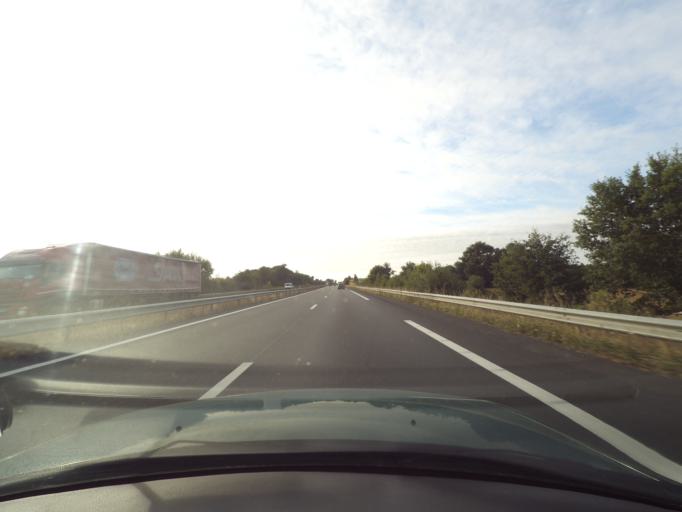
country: FR
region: Pays de la Loire
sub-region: Departement de Maine-et-Loire
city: Saint-Andre-de-la-Marche
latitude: 47.1005
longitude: -1.0218
